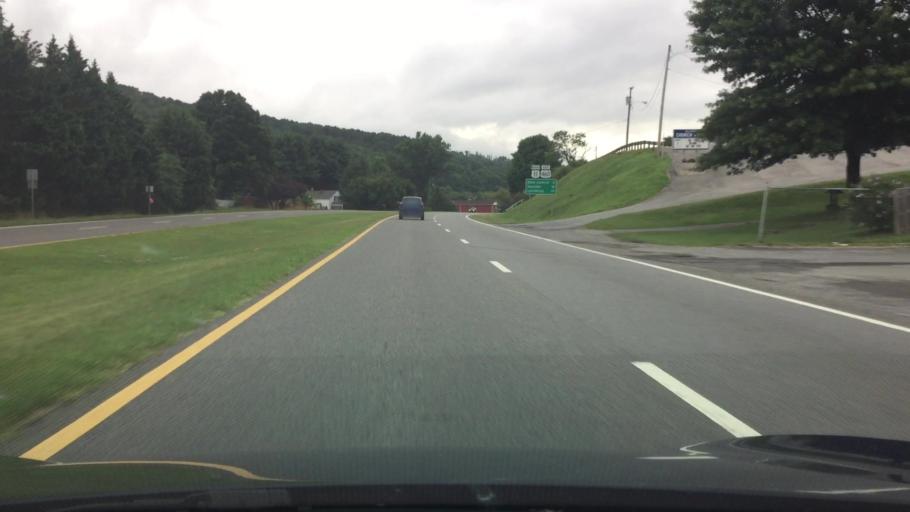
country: US
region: Virginia
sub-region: Montgomery County
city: Shawsville
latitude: 37.2173
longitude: -80.2312
